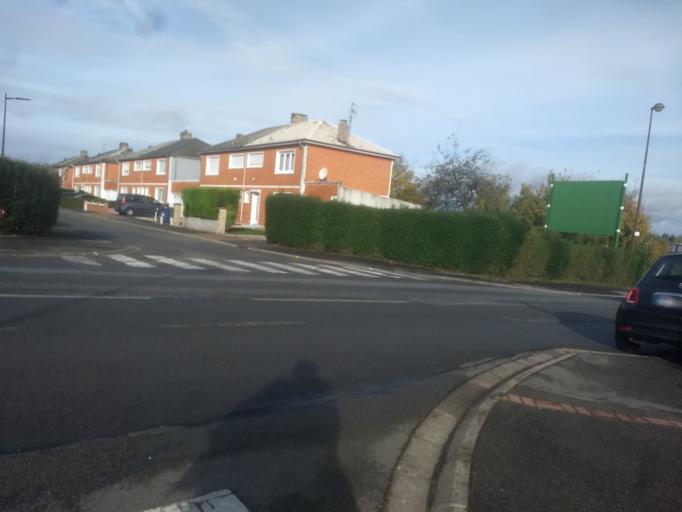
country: FR
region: Nord-Pas-de-Calais
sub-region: Departement du Pas-de-Calais
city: Dainville
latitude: 50.2956
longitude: 2.7304
